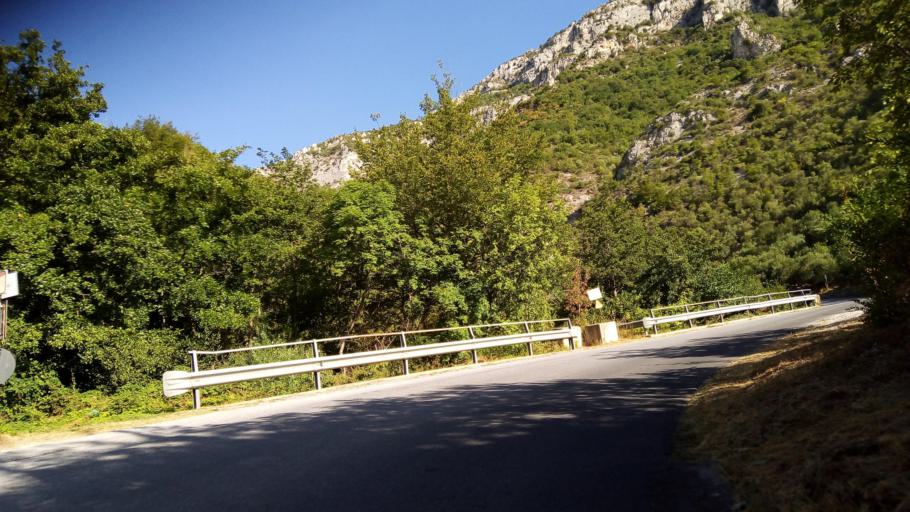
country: IT
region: Liguria
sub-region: Provincia di Savona
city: Toirano
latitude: 44.1361
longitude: 8.1973
